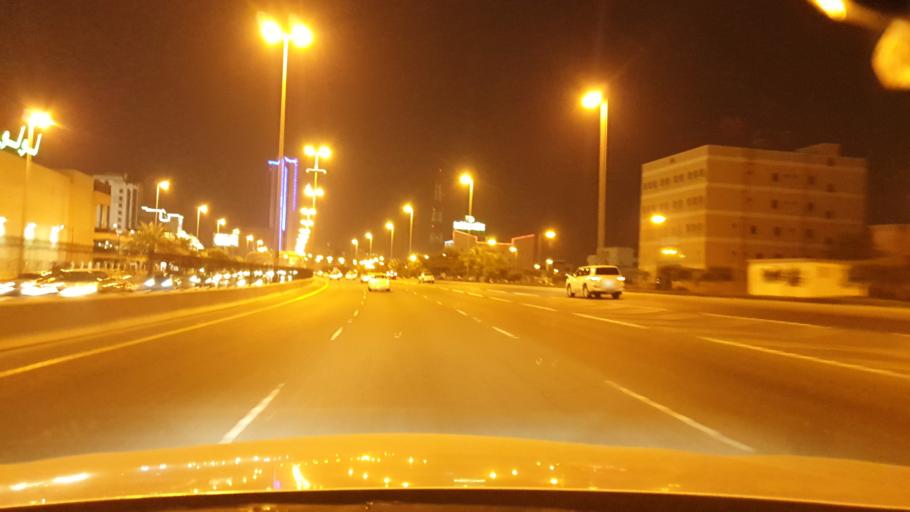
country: BH
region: Manama
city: Manama
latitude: 26.2033
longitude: 50.5723
